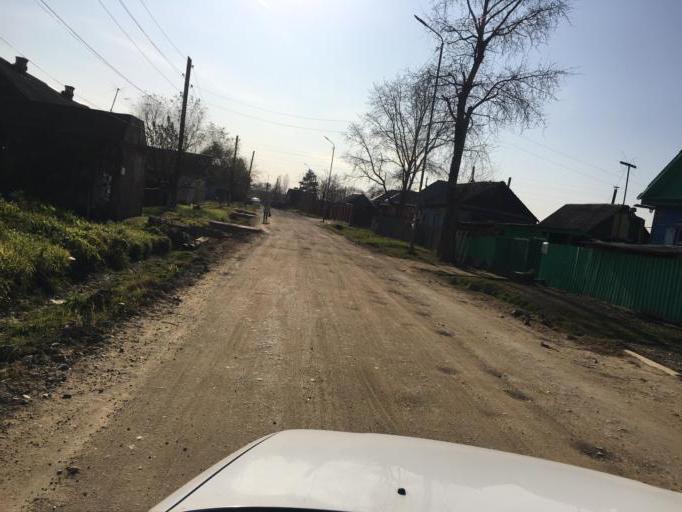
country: RU
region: Primorskiy
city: Dal'nerechensk
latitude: 45.9212
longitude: 133.7246
